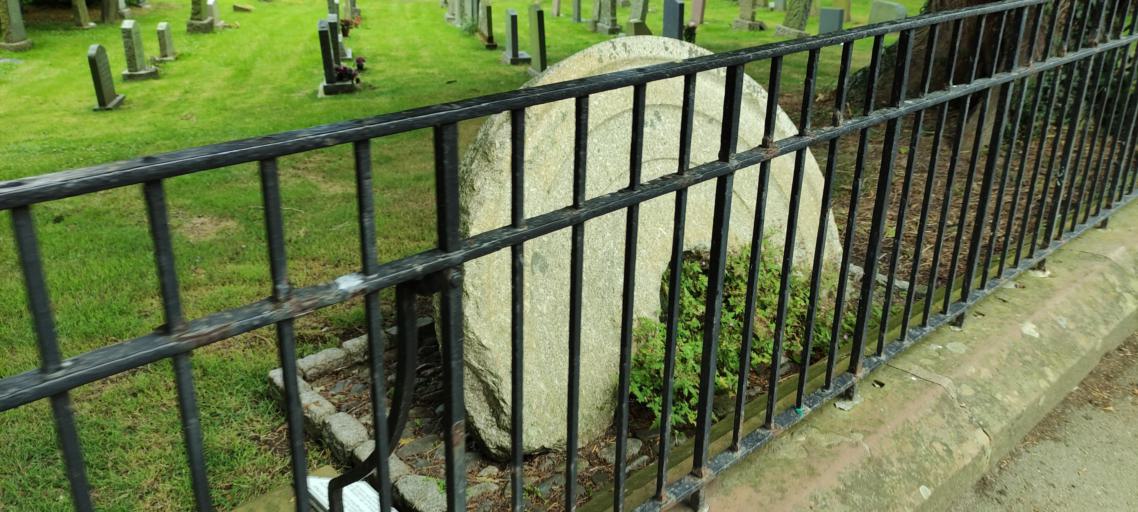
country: GB
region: England
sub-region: Cumbria
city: Wigton
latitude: 54.7486
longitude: -3.0495
